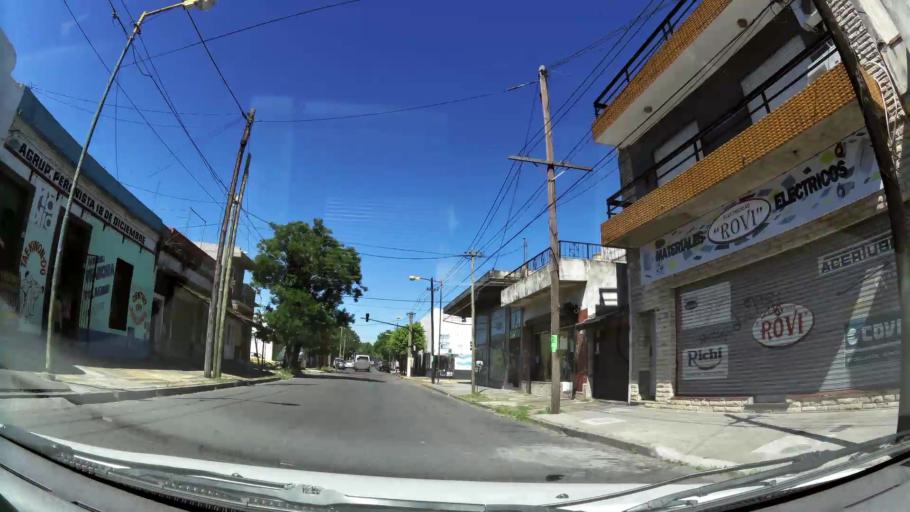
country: AR
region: Buenos Aires
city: Caseros
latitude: -34.5834
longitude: -58.5463
